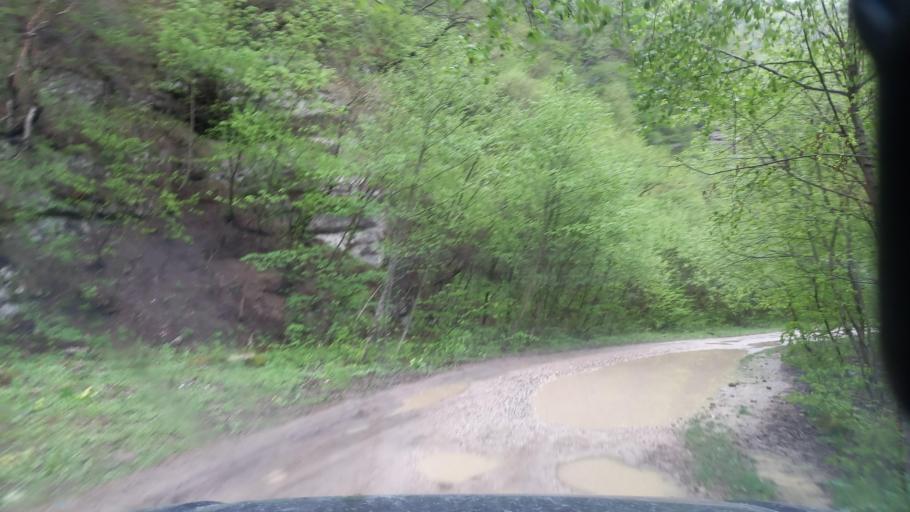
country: RU
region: Kabardino-Balkariya
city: Bylym
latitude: 43.5891
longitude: 43.0224
